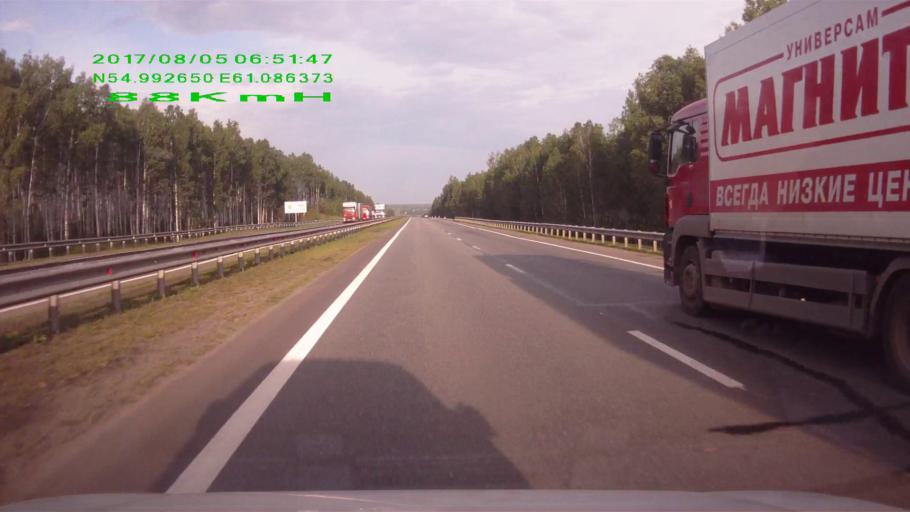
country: RU
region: Chelyabinsk
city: Poletayevo
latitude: 54.9926
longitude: 61.0859
